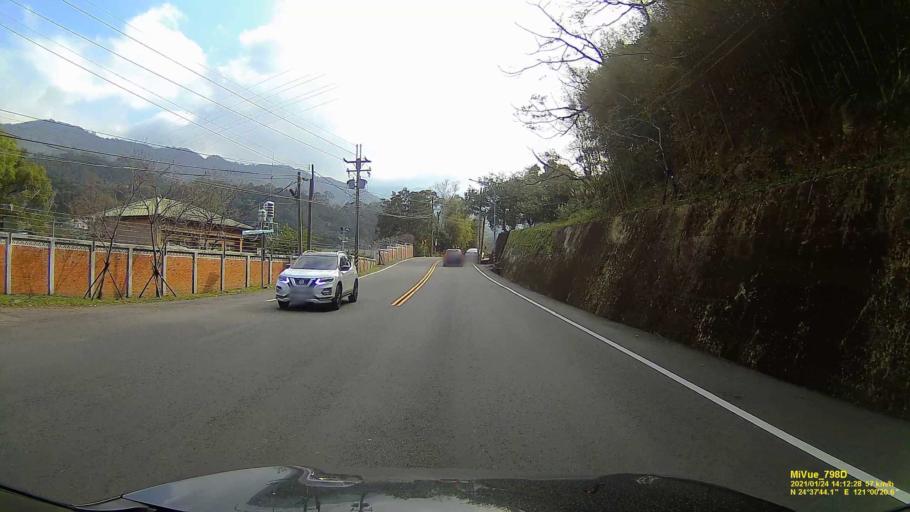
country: TW
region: Taiwan
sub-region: Hsinchu
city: Hsinchu
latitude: 24.6285
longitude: 121.0057
